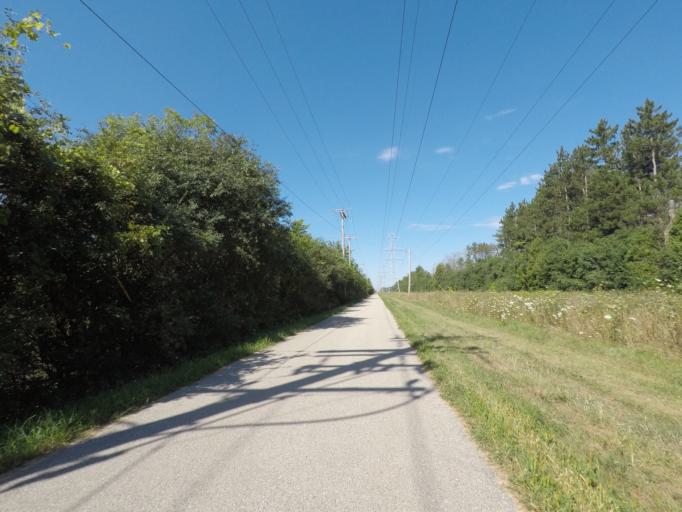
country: US
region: Wisconsin
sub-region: Waukesha County
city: New Berlin
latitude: 43.0101
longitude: -88.1374
